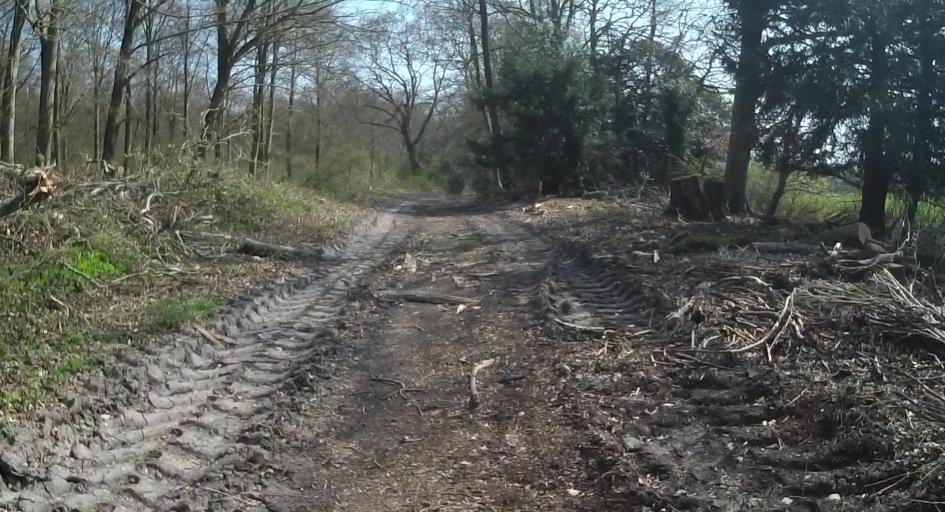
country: GB
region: England
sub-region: Hampshire
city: Overton
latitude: 51.1884
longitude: -1.2464
